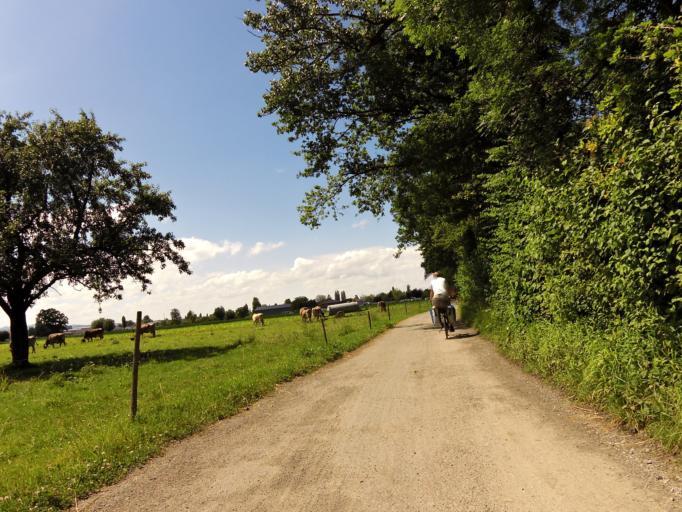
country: CH
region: Saint Gallen
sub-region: Wahlkreis Rheintal
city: Rheineck
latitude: 47.4885
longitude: 9.5693
